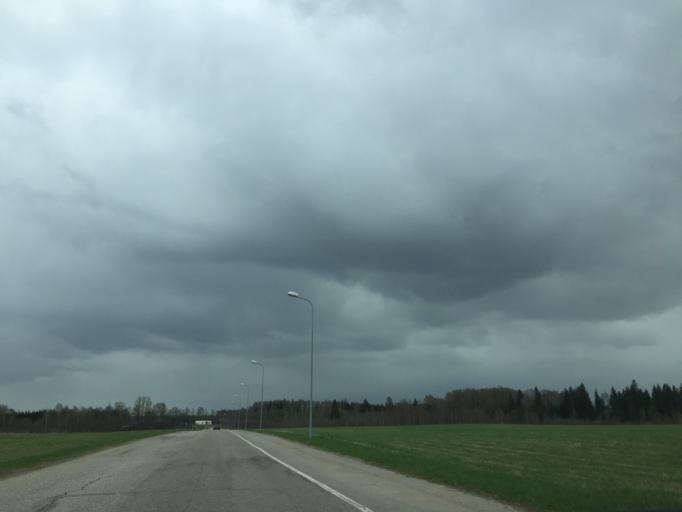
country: LV
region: Priekuli
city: Priekuli
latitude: 57.3483
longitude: 25.3311
